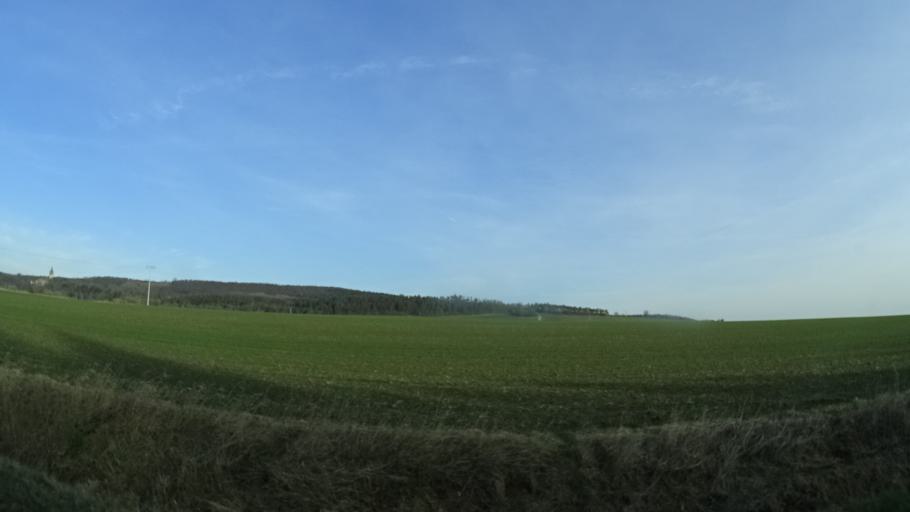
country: DE
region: Thuringia
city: Tonndorf
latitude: 50.8851
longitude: 11.2211
